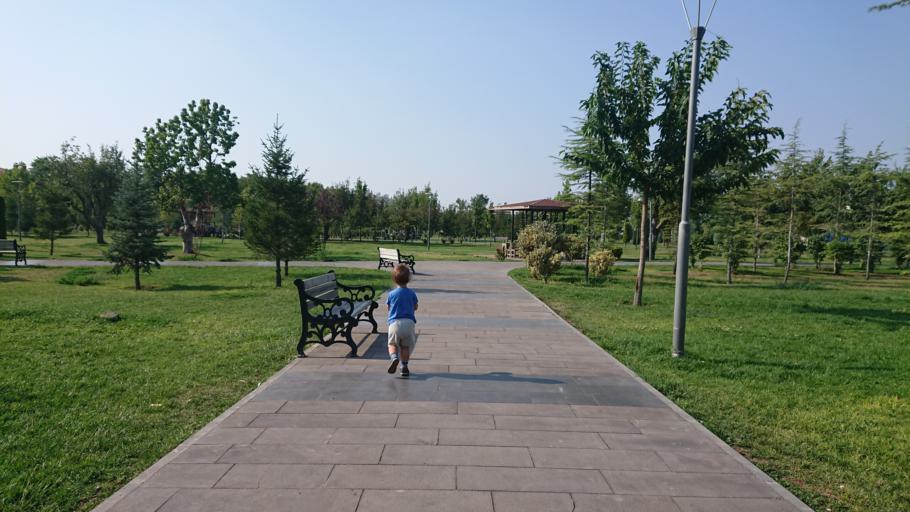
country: TR
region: Eskisehir
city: Eskisehir
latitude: 39.7644
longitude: 30.4957
